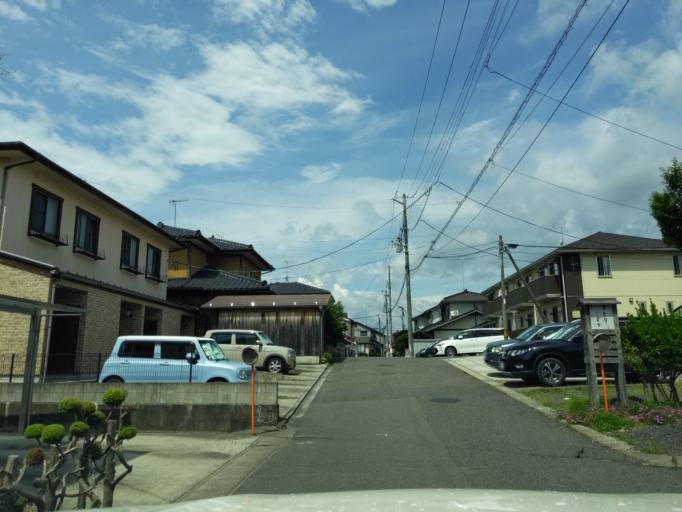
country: JP
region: Fukushima
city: Koriyama
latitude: 37.3764
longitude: 140.3591
